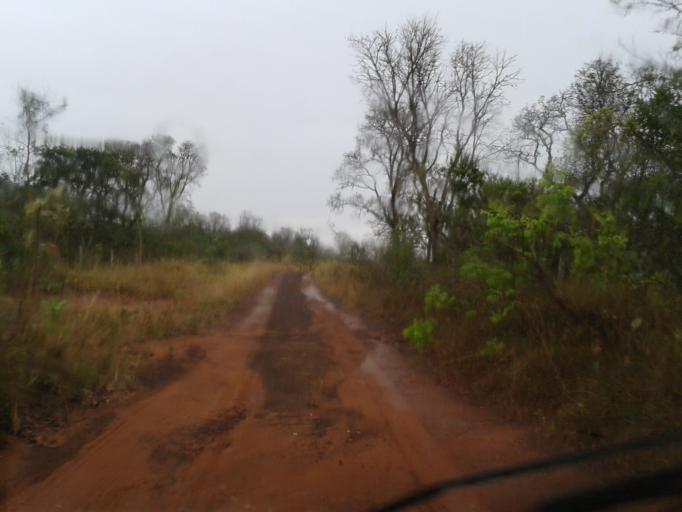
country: BR
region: Minas Gerais
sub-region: Campina Verde
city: Campina Verde
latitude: -19.3283
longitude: -49.5157
